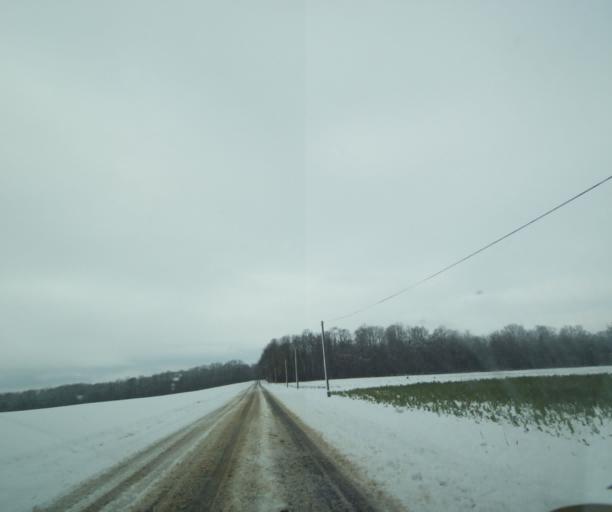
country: FR
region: Champagne-Ardenne
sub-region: Departement de la Haute-Marne
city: Montier-en-Der
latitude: 48.5307
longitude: 4.7415
